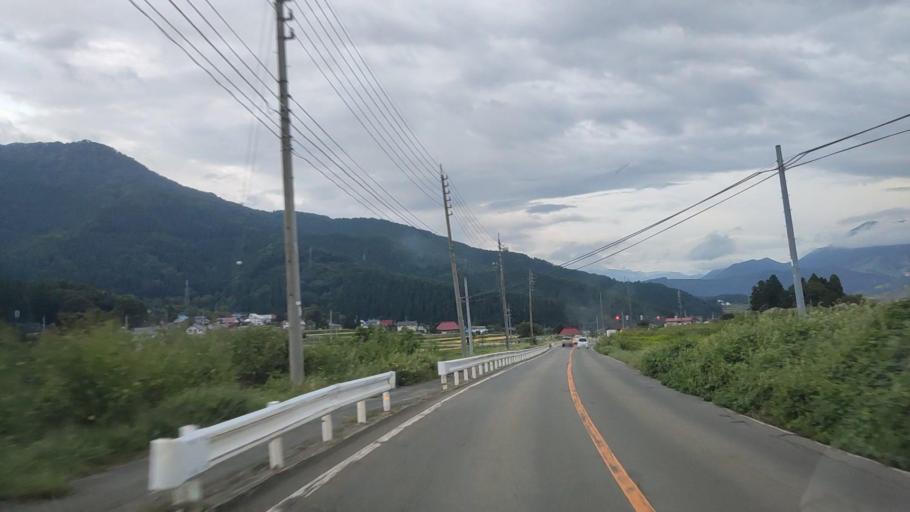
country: JP
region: Nagano
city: Iiyama
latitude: 36.8847
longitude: 138.4119
